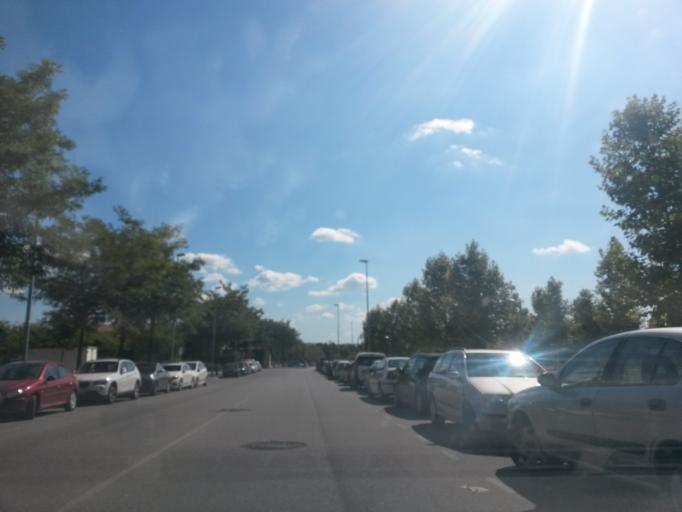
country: ES
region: Catalonia
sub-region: Provincia de Girona
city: Salt
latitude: 41.9705
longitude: 2.8011
